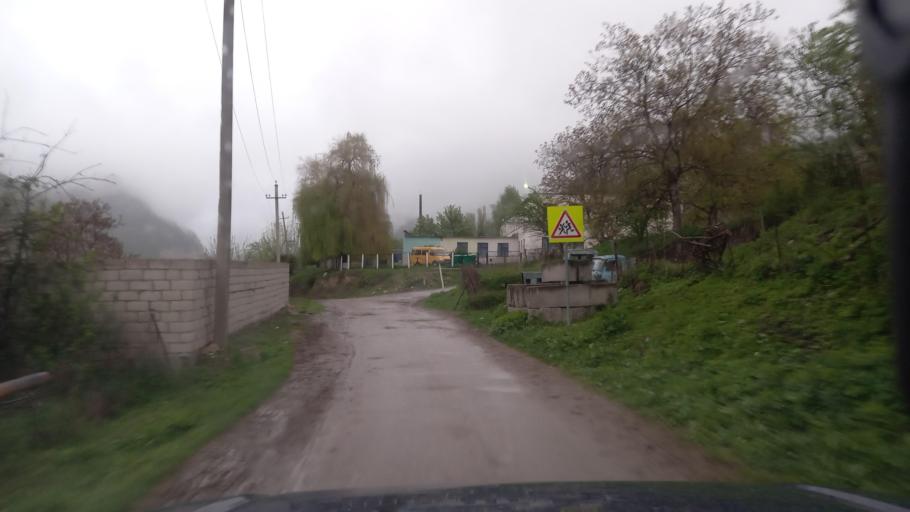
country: RU
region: Kabardino-Balkariya
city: Zhankhoteko
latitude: 43.5116
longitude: 43.1562
